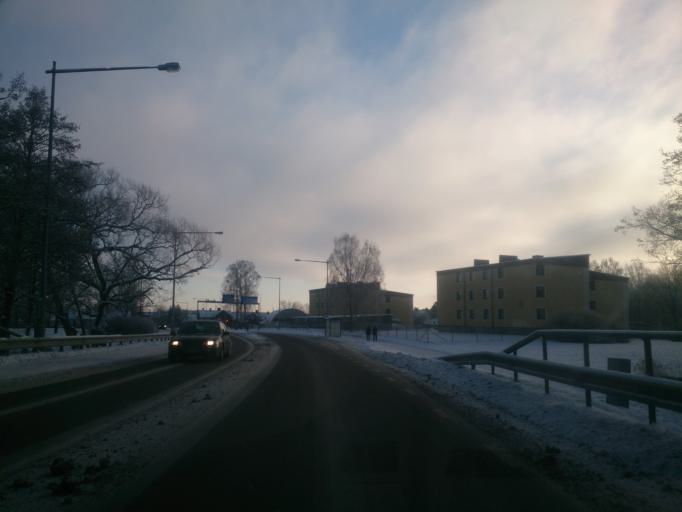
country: SE
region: OEstergoetland
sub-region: Soderkopings Kommun
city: Soederkoeping
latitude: 58.4803
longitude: 16.3143
